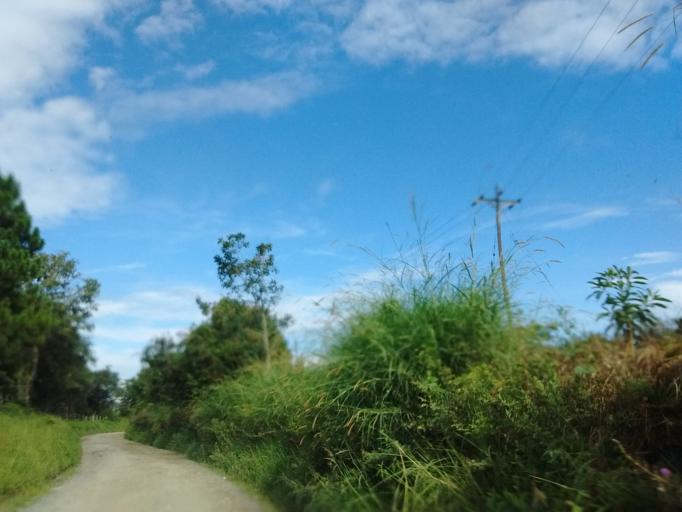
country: CO
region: Cauca
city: Cajibio
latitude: 2.6200
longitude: -76.5854
